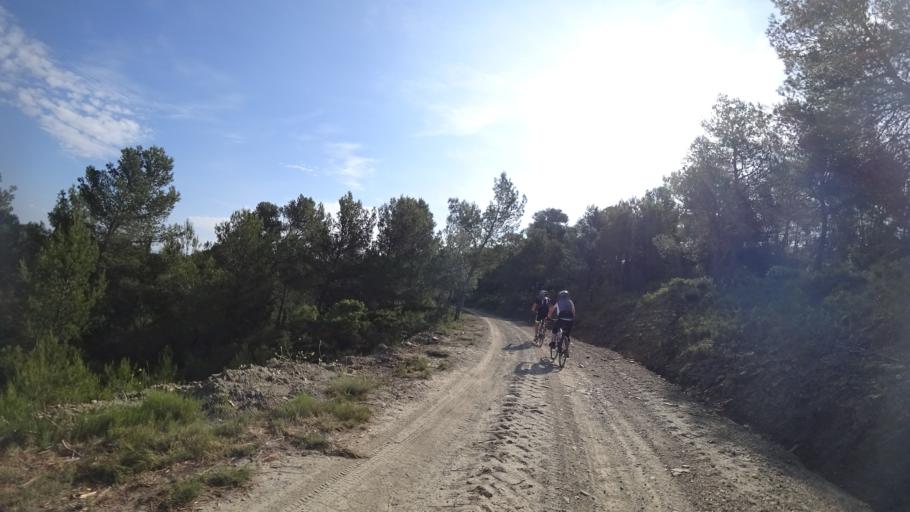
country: FR
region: Languedoc-Roussillon
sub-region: Departement de l'Herault
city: Olonzac
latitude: 43.2484
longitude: 2.7259
